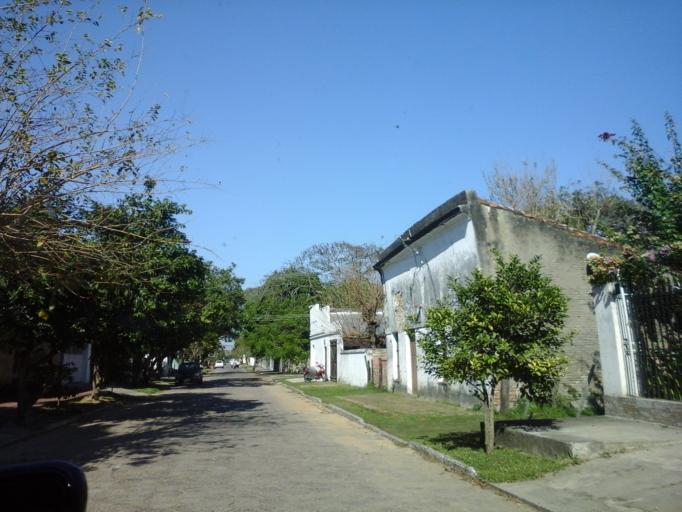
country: PY
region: Neembucu
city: Pilar
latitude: -26.8523
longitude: -58.3069
